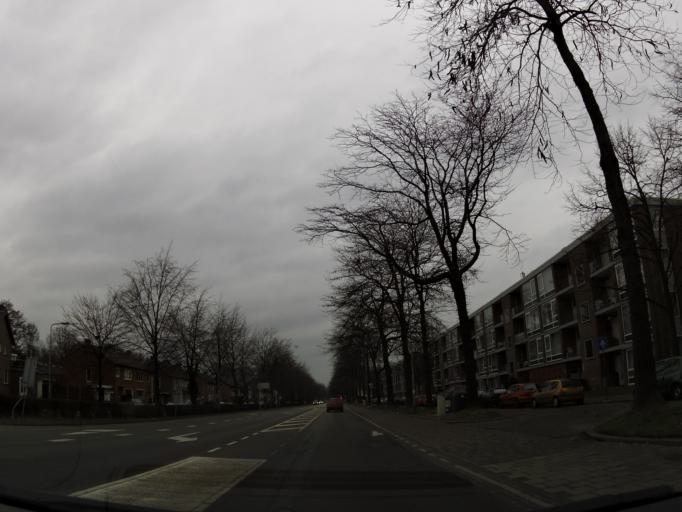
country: NL
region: Limburg
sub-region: Gemeente Sittard-Geleen
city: Sittard
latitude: 51.0025
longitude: 5.8691
